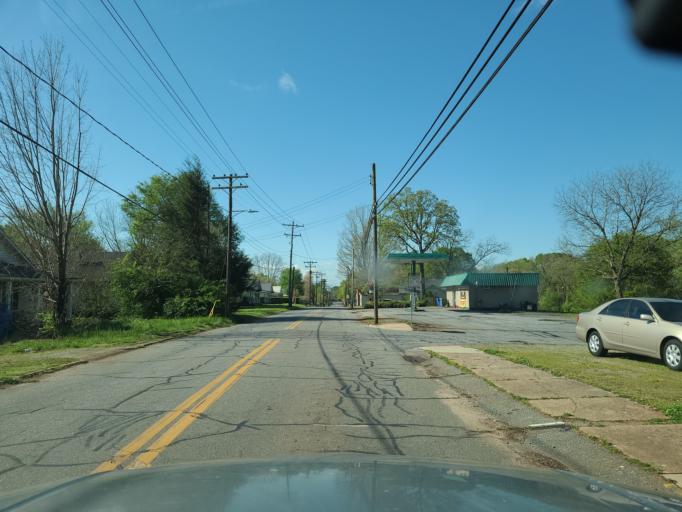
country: US
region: North Carolina
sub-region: Rutherford County
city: Spindale
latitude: 35.3680
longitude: -81.9271
